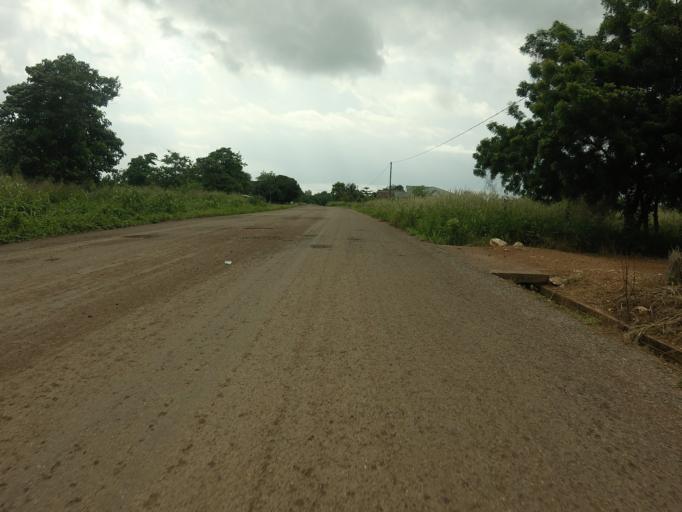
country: GH
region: Volta
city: Kpandu
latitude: 6.9486
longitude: 0.4597
